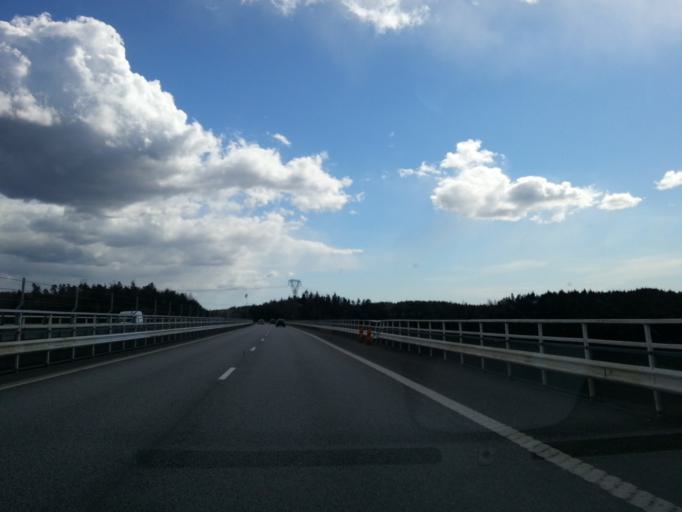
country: SE
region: Vaestra Goetaland
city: Svanesund
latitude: 58.1111
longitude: 11.8789
